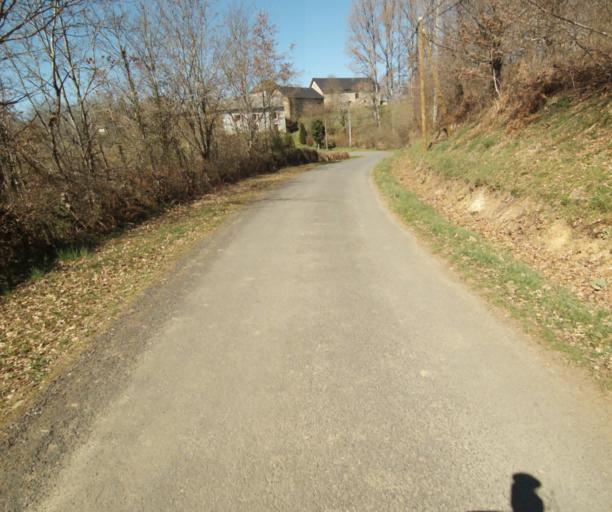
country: FR
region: Limousin
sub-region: Departement de la Correze
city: Saint-Clement
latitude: 45.3264
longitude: 1.7062
